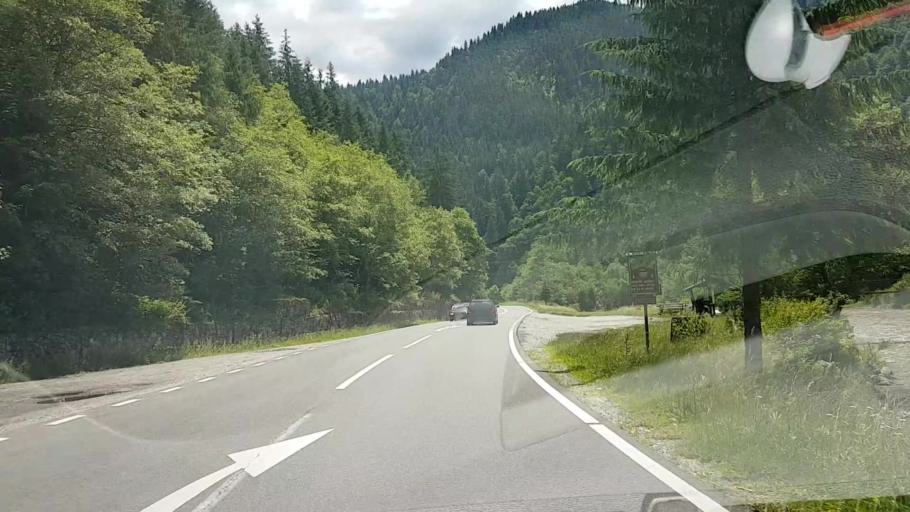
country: RO
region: Suceava
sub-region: Comuna Brosteni
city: Brosteni
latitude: 47.2608
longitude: 25.6687
